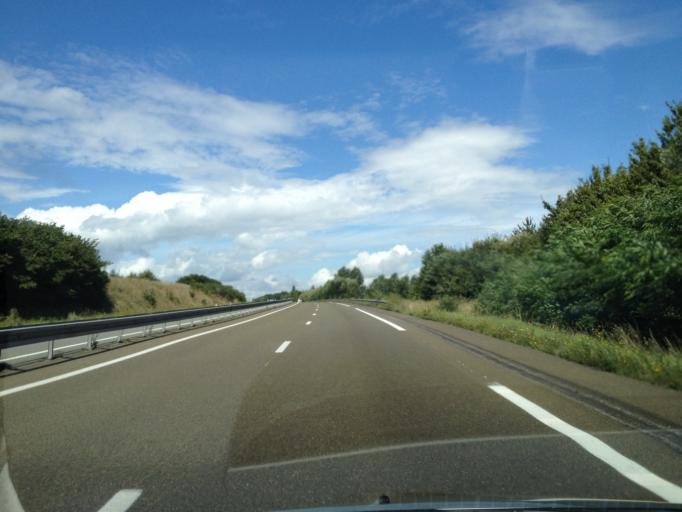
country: FR
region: Pays de la Loire
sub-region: Departement de la Sarthe
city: Neuville-sur-Sarthe
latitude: 48.0875
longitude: 0.1767
